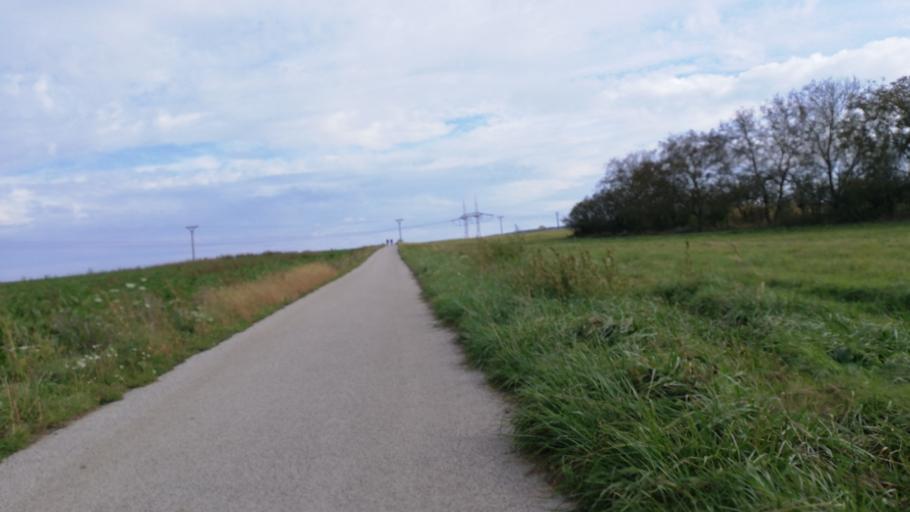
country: CZ
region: South Moravian
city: Sudomerice
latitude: 48.8498
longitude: 17.2559
